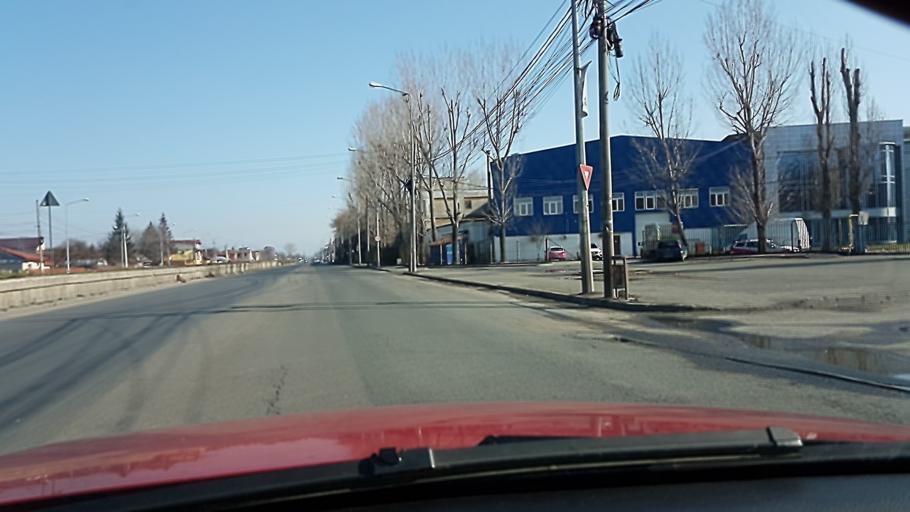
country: RO
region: Ilfov
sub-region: Comuna Pantelimon
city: Pantelimon
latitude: 44.4319
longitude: 26.1933
